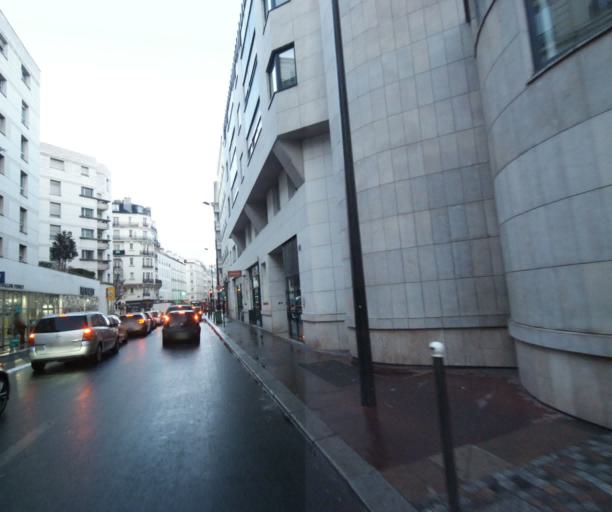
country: FR
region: Ile-de-France
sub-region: Departement des Hauts-de-Seine
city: Levallois-Perret
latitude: 48.8950
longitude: 2.2976
